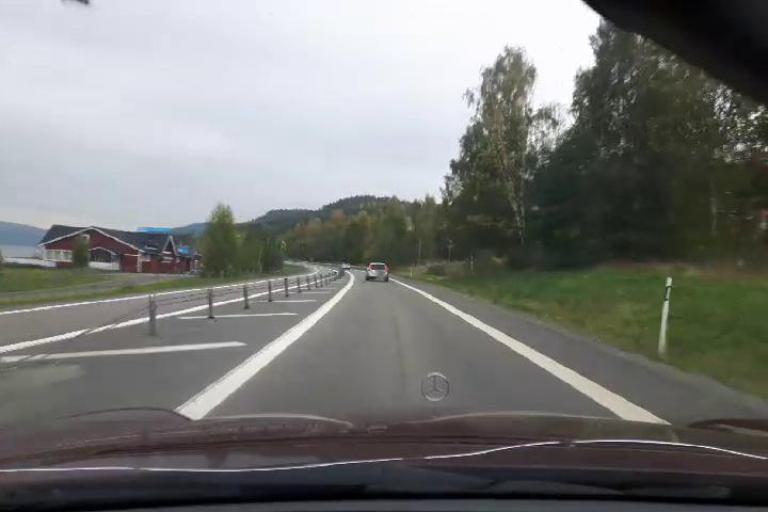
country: SE
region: Vaesternorrland
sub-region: Kramfors Kommun
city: Nordingra
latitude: 63.0477
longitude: 18.3257
